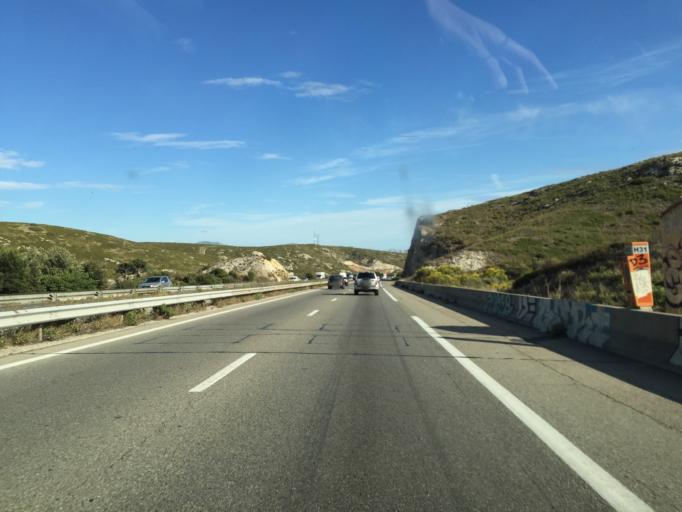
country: FR
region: Provence-Alpes-Cote d'Azur
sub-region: Departement des Bouches-du-Rhone
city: Marseille 16
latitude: 43.3791
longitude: 5.3167
